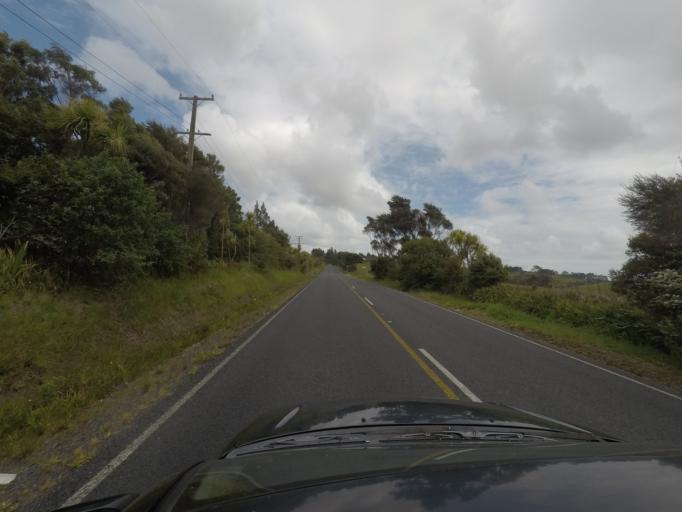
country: NZ
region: Auckland
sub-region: Auckland
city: Parakai
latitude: -36.6324
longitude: 174.5040
